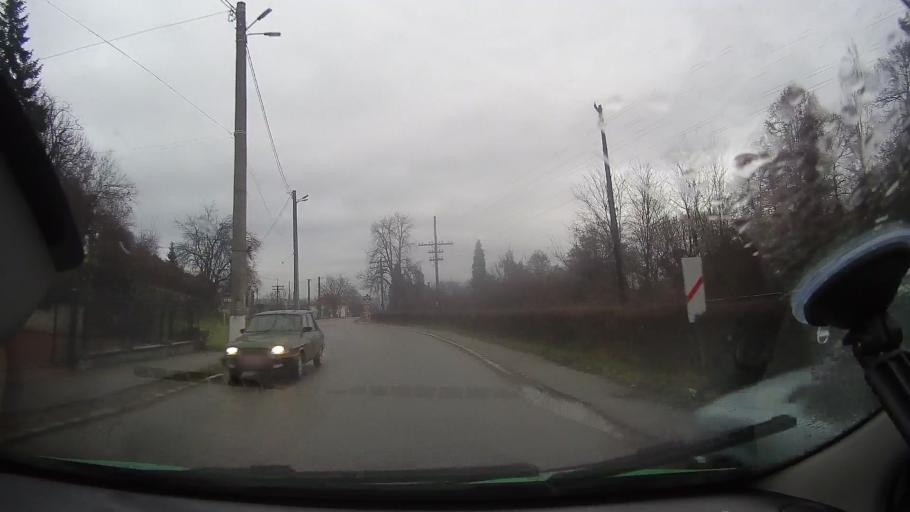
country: RO
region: Hunedoara
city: Vata de Jos
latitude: 46.1798
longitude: 22.6011
